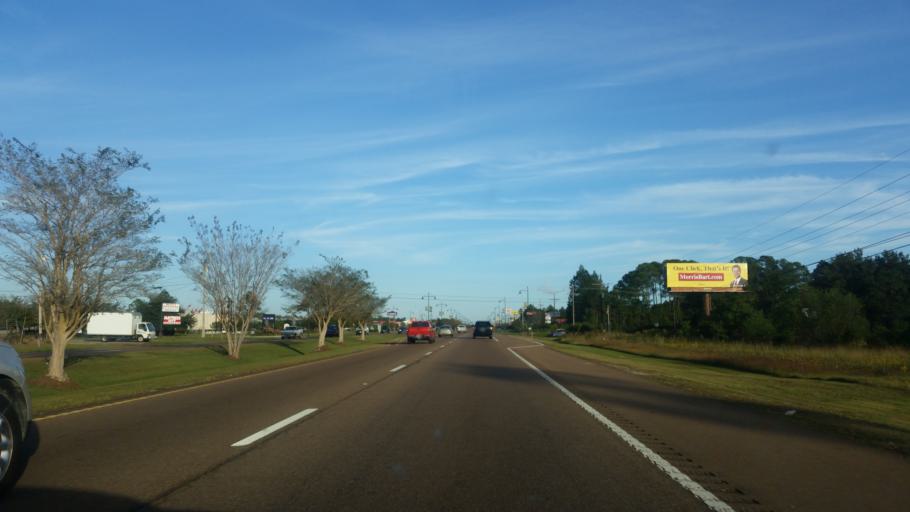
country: US
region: Mississippi
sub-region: Jackson County
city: Gautier
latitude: 30.3940
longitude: -88.6665
